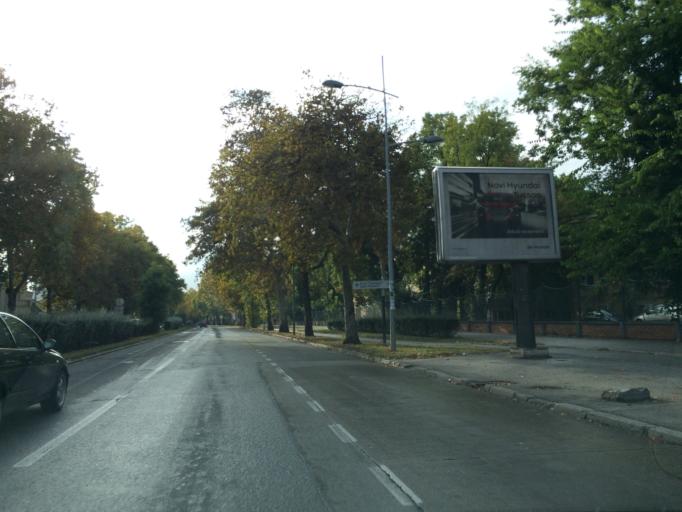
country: RS
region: Autonomna Pokrajina Vojvodina
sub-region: Juznobacki Okrug
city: Novi Sad
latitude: 45.2493
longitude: 19.8240
